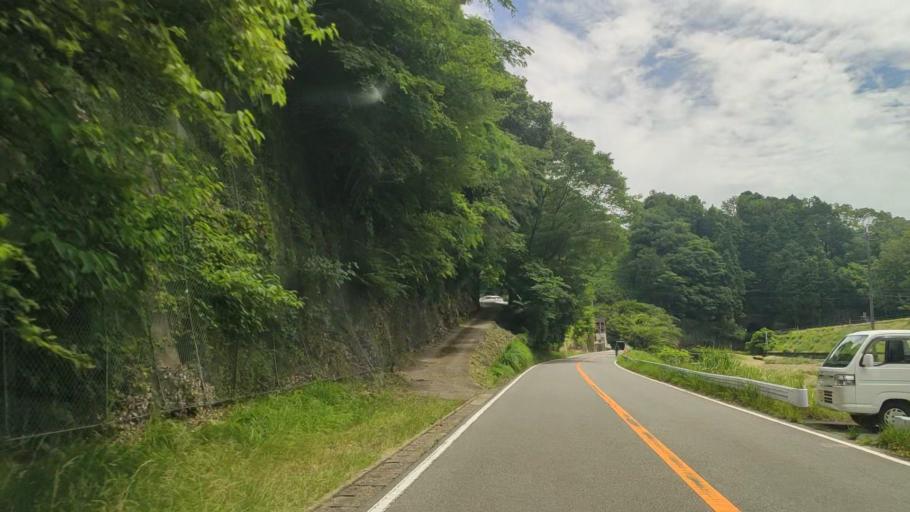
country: JP
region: Hyogo
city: Yamazakicho-nakabirose
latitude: 35.0763
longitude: 134.3594
